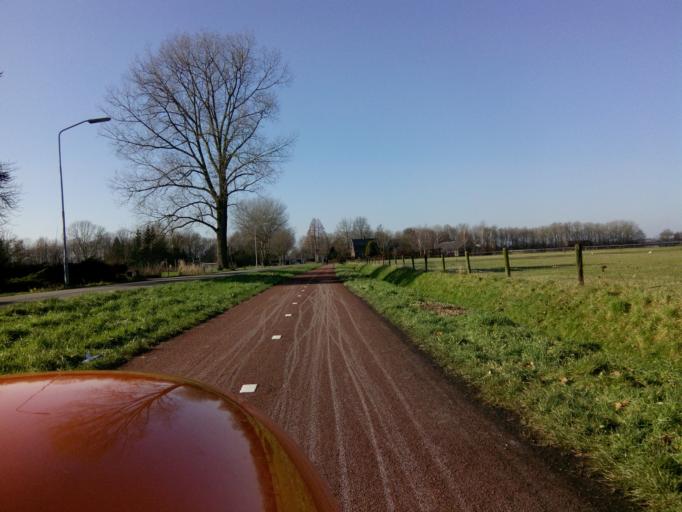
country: NL
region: Gelderland
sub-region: Gemeente Barneveld
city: Barneveld
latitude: 52.1326
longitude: 5.5670
